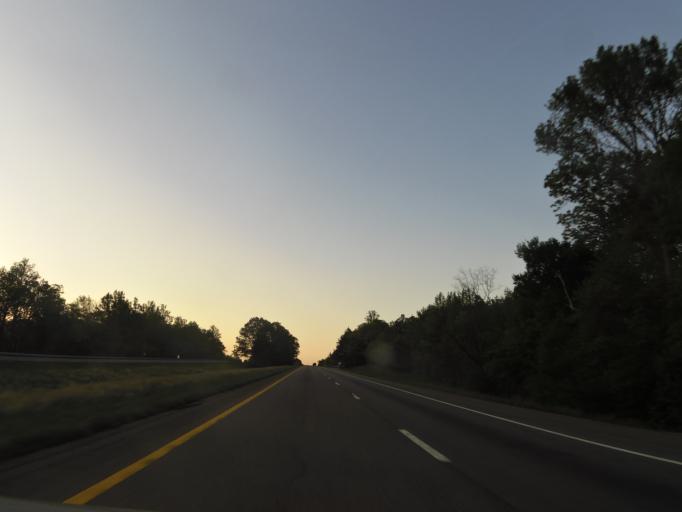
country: US
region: Tennessee
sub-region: Cocke County
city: Newport
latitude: 35.8597
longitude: -83.1839
